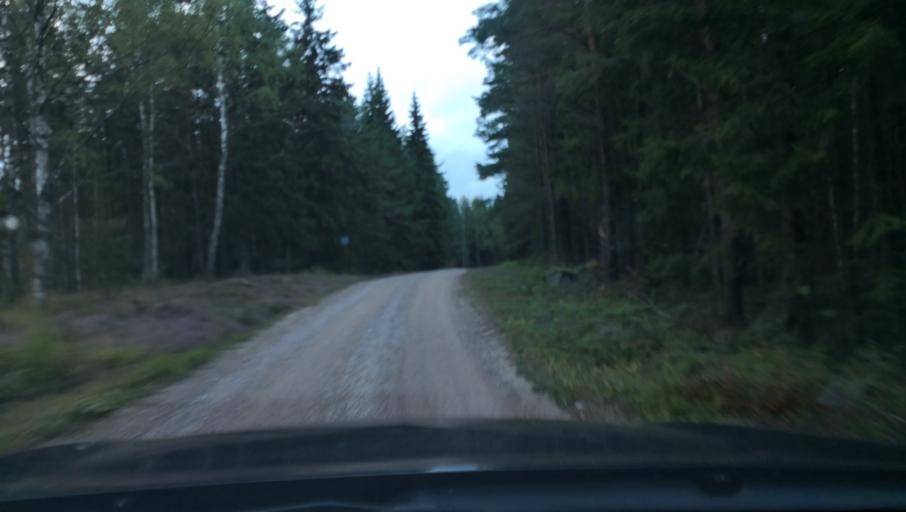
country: SE
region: Vaestmanland
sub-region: Arboga Kommun
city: Tyringe
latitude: 59.3508
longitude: 15.9985
